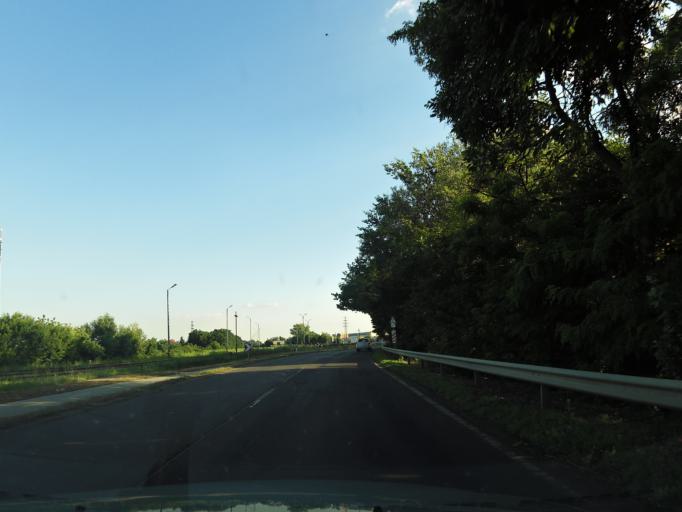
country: HU
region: Jasz-Nagykun-Szolnok
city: Rakocziujfalu
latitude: 47.0249
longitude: 20.2927
